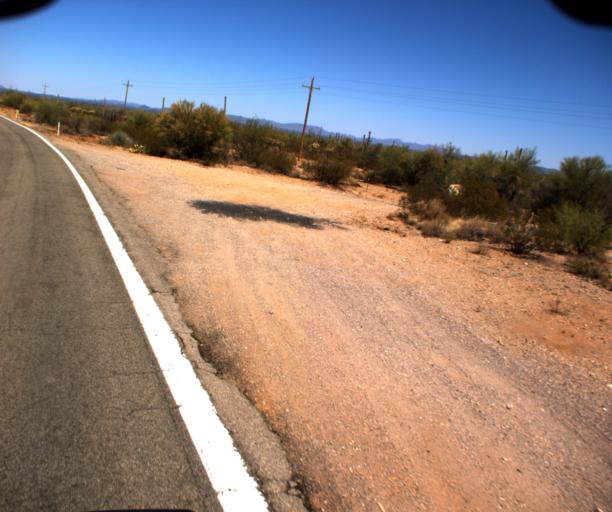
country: US
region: Arizona
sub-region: Pima County
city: Sells
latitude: 32.1818
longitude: -112.2810
